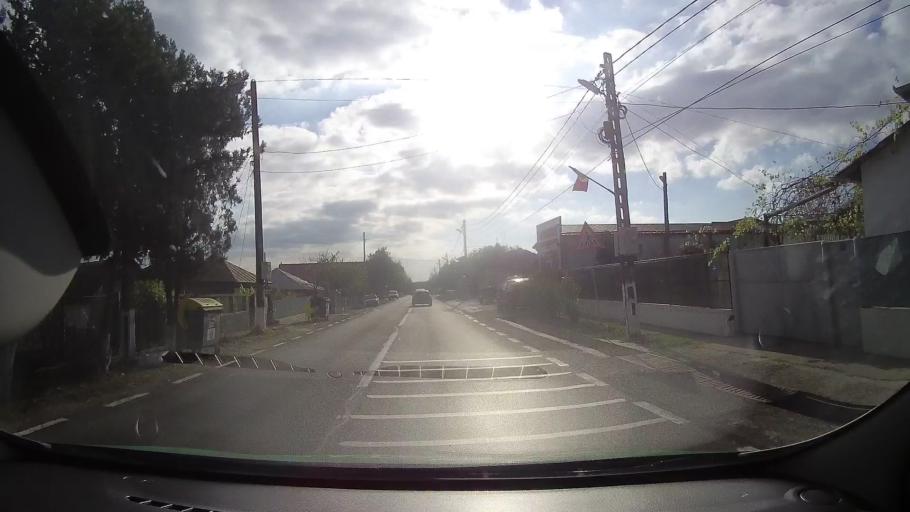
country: RO
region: Tulcea
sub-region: Comuna Topolog
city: Topolog
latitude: 44.8787
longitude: 28.3754
